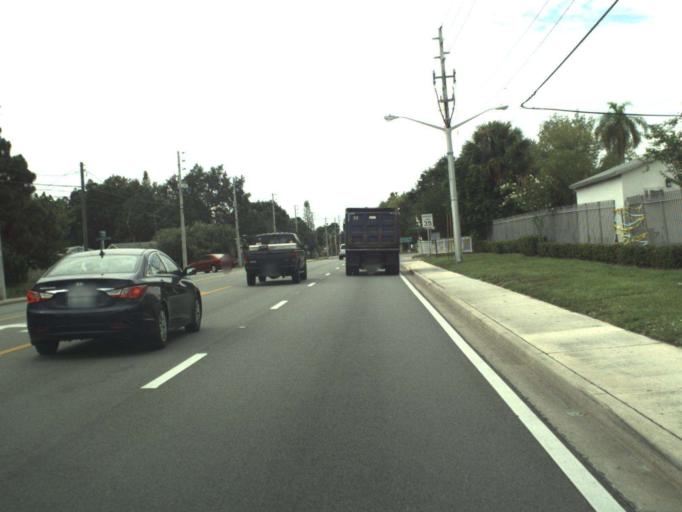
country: US
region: Florida
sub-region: Saint Lucie County
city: Fort Pierce
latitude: 27.4409
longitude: -80.3500
